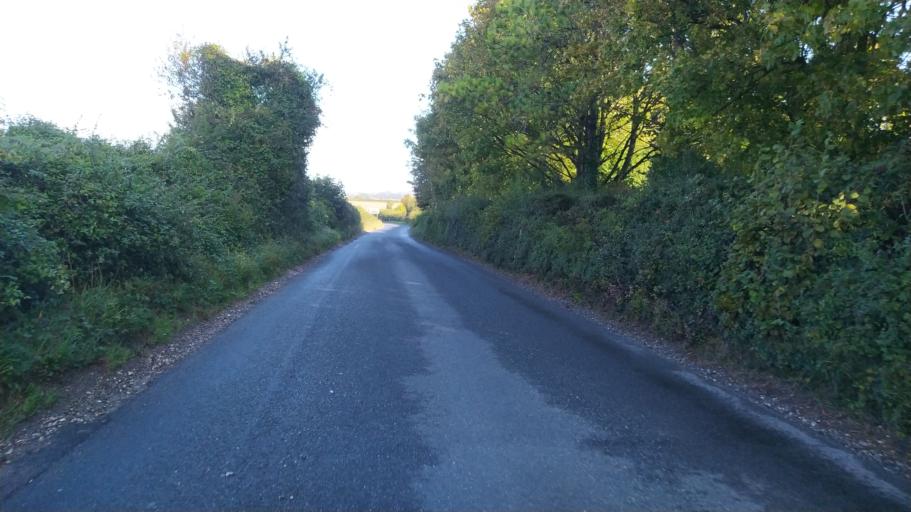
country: GB
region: England
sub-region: Wiltshire
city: Ansty
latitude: 50.9237
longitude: -2.0549
